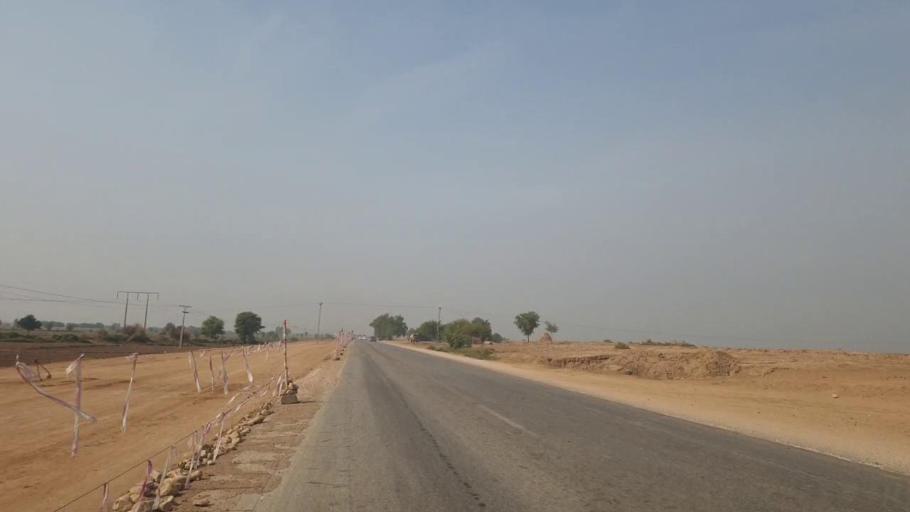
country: PK
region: Sindh
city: Sann
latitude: 26.1330
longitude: 68.0468
